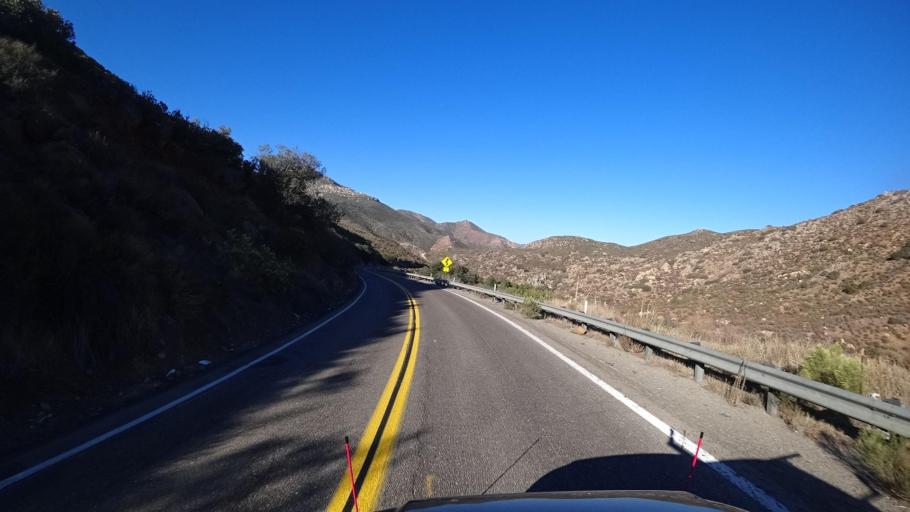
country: MX
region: Baja California
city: Tecate
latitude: 32.5972
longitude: -116.6556
